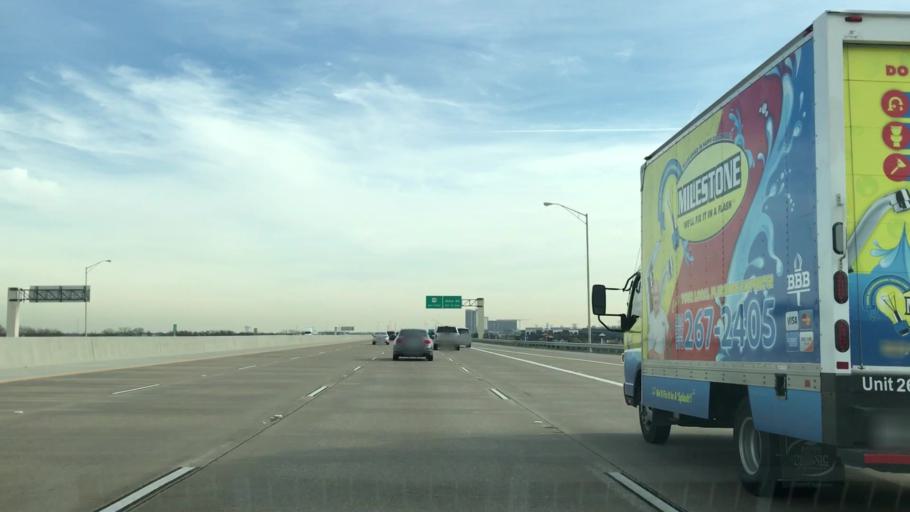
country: US
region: Texas
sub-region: Collin County
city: Plano
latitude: 33.0037
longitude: -96.7358
